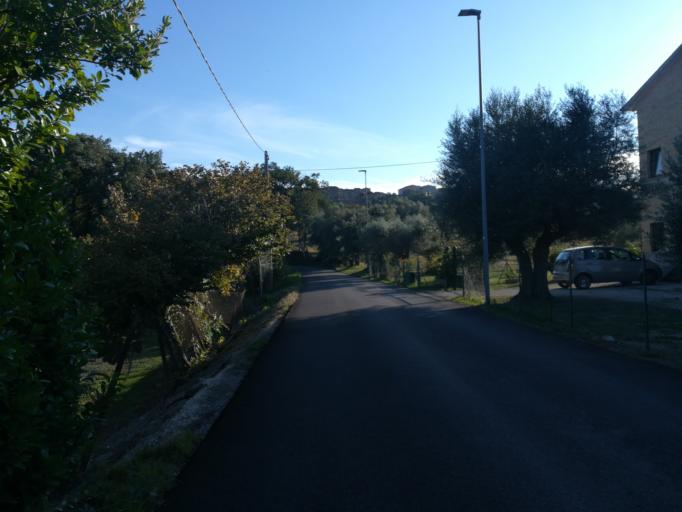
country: IT
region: The Marches
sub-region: Provincia di Macerata
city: Macerata
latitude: 43.3066
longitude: 13.4528
